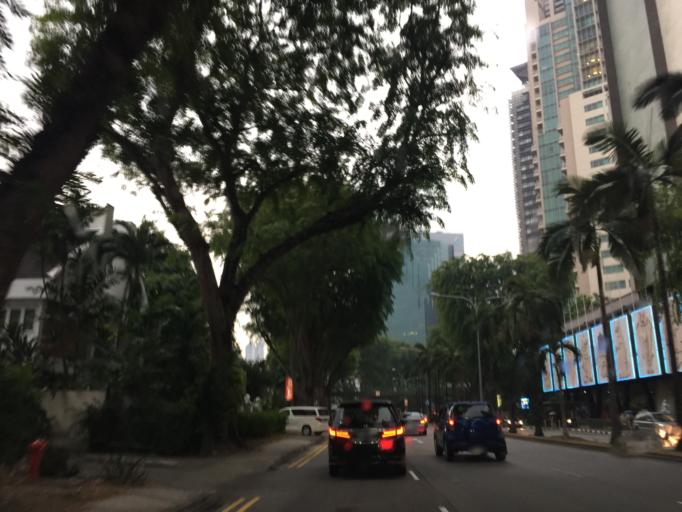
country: SG
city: Singapore
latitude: 1.3163
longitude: 103.8412
